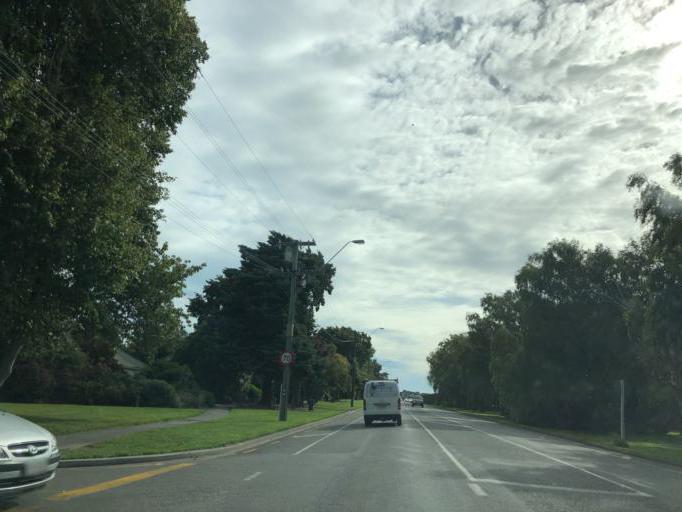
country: NZ
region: Canterbury
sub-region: Selwyn District
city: Lincoln
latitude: -43.6425
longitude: 172.4655
